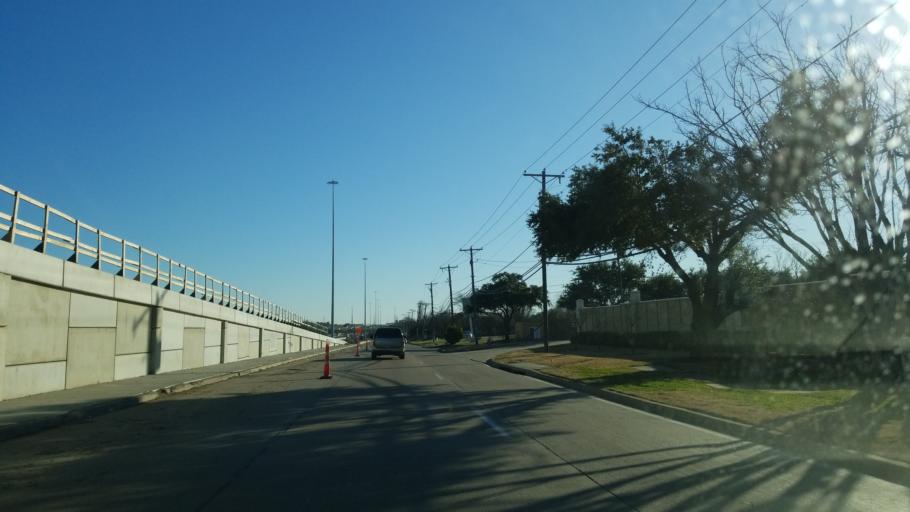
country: US
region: Texas
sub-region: Tarrant County
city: Arlington
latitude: 32.7339
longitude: -97.0630
